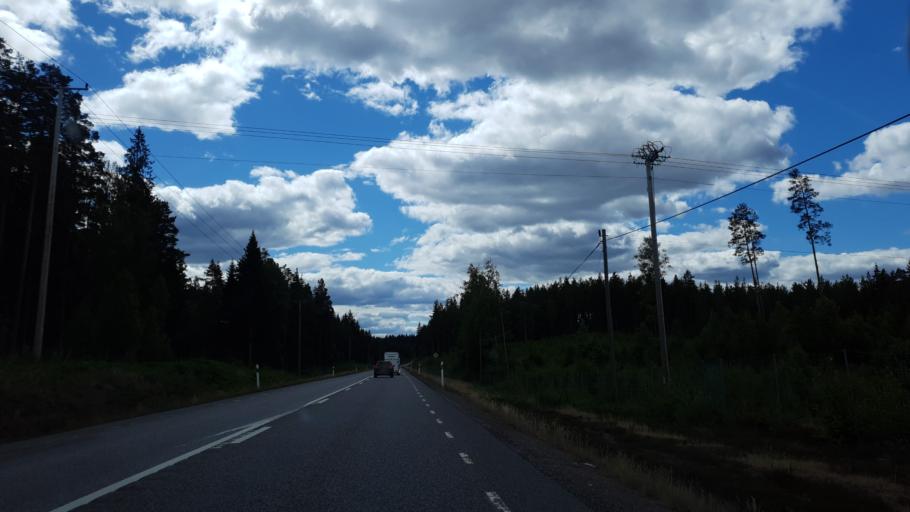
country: SE
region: Kronoberg
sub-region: Vaxjo Kommun
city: Braas
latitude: 57.1799
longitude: 15.1583
